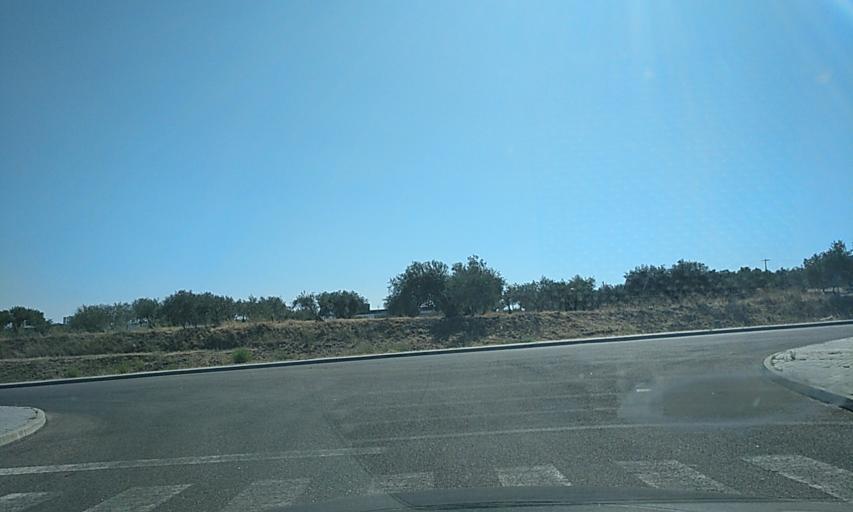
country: PT
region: Portalegre
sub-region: Campo Maior
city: Campo Maior
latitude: 39.0249
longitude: -7.0626
